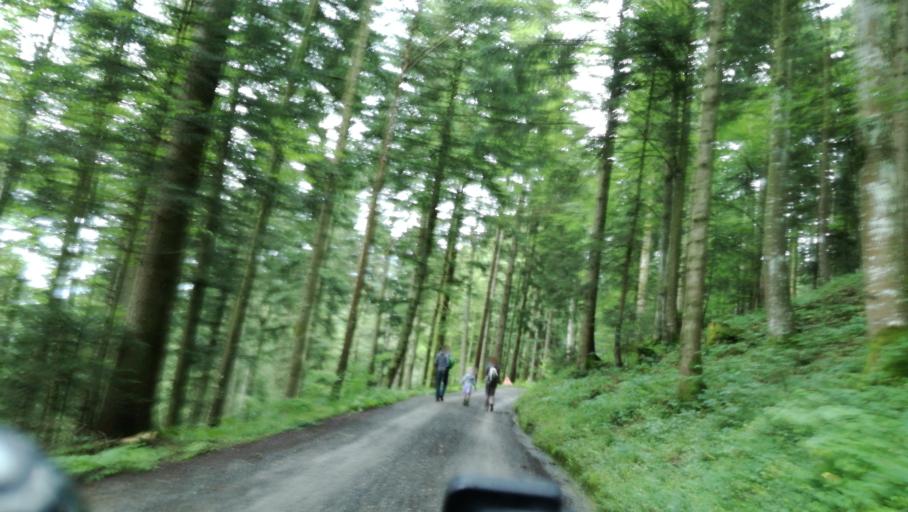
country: CH
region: Zug
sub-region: Zug
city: Unterageri
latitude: 47.0980
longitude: 8.5627
